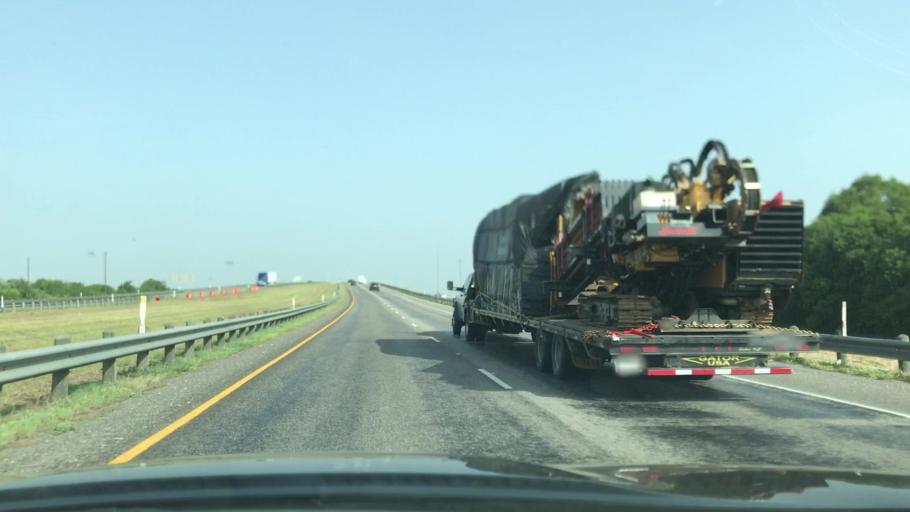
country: US
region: Texas
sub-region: Kaufman County
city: Talty
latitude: 32.7359
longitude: -96.3511
